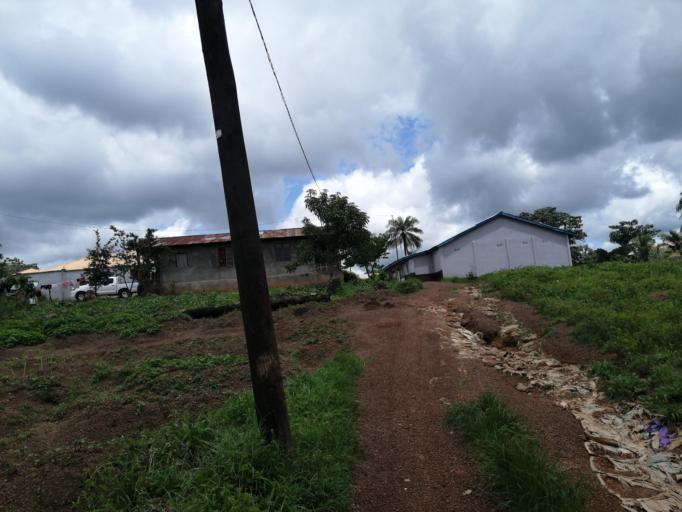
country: SL
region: Northern Province
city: Port Loko
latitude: 8.7722
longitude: -12.7802
